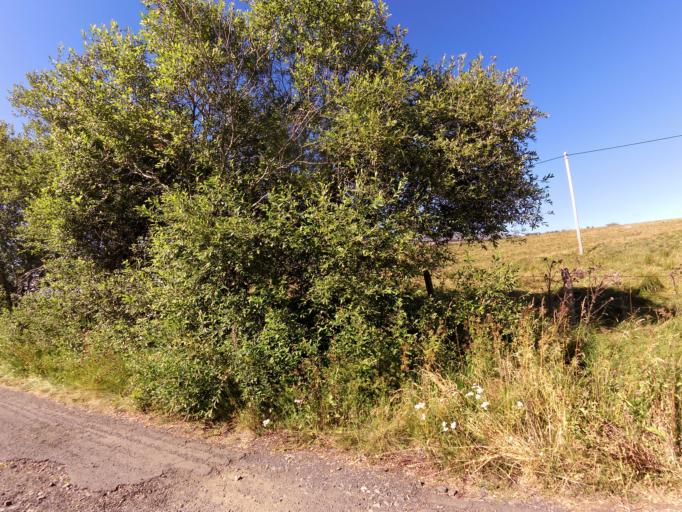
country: FR
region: Auvergne
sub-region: Departement du Cantal
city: Allanche
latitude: 45.3877
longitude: 2.9254
